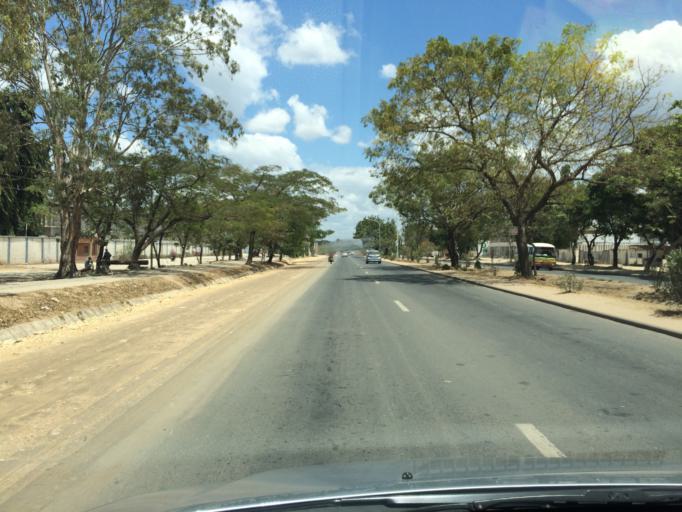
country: TZ
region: Dar es Salaam
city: Dar es Salaam
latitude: -6.8421
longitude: 39.2499
